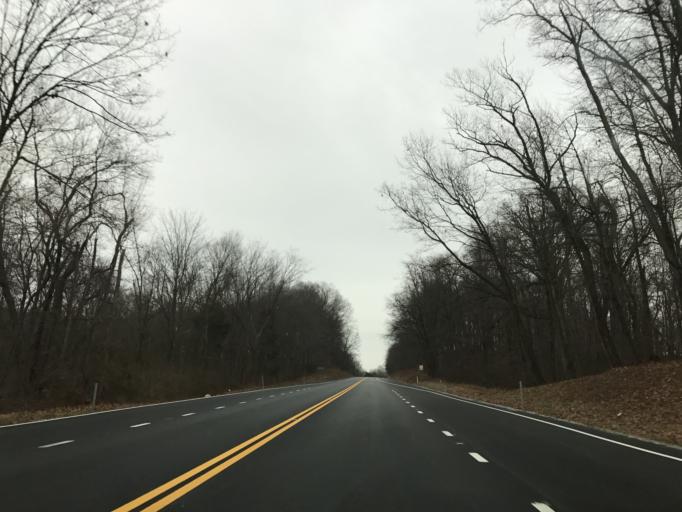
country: US
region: Maryland
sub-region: Carroll County
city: New Windsor
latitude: 39.6198
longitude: -77.0911
